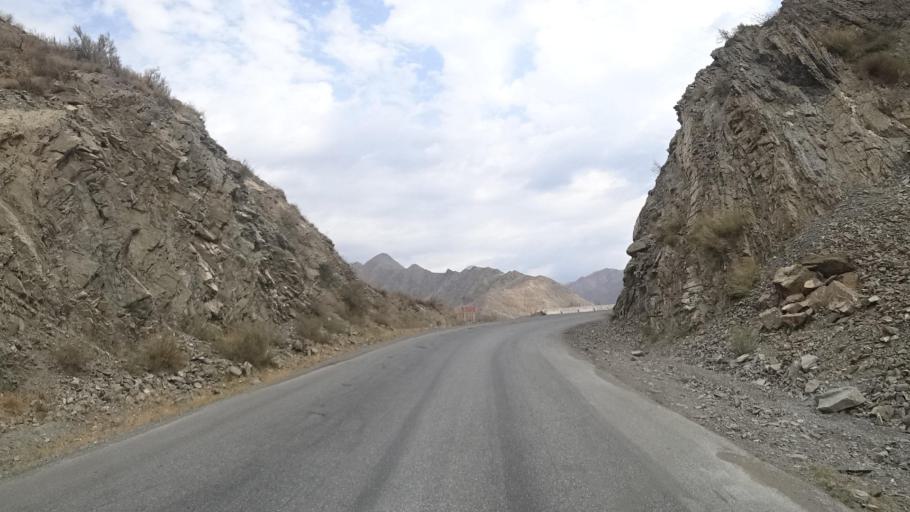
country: KG
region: Jalal-Abad
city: Tash-Kumyr
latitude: 41.5038
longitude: 72.3779
